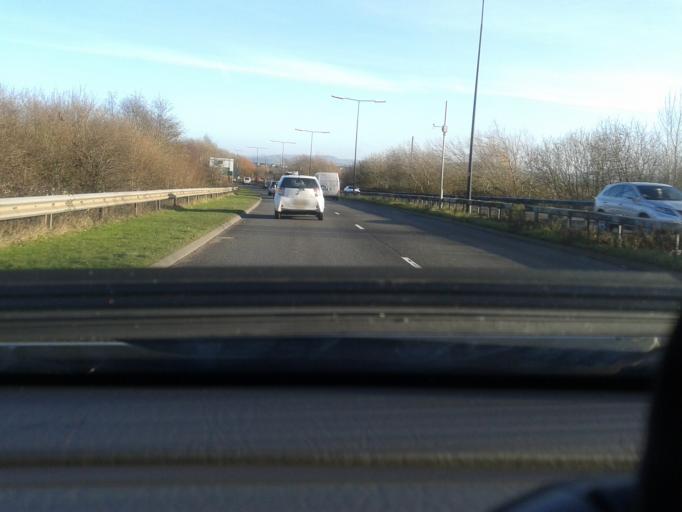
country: GB
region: England
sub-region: North Somerset
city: Hutton
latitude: 51.3452
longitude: -2.9362
